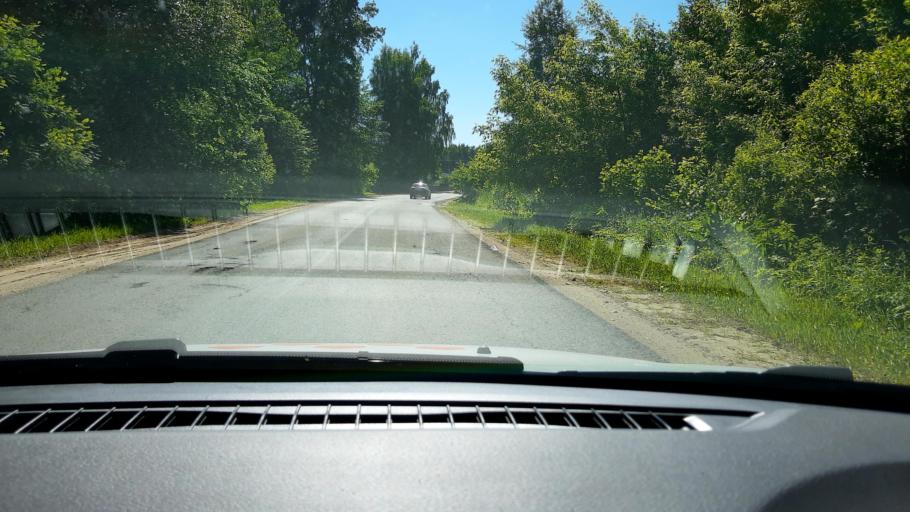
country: RU
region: Nizjnij Novgorod
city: Bor
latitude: 56.3857
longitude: 44.1537
